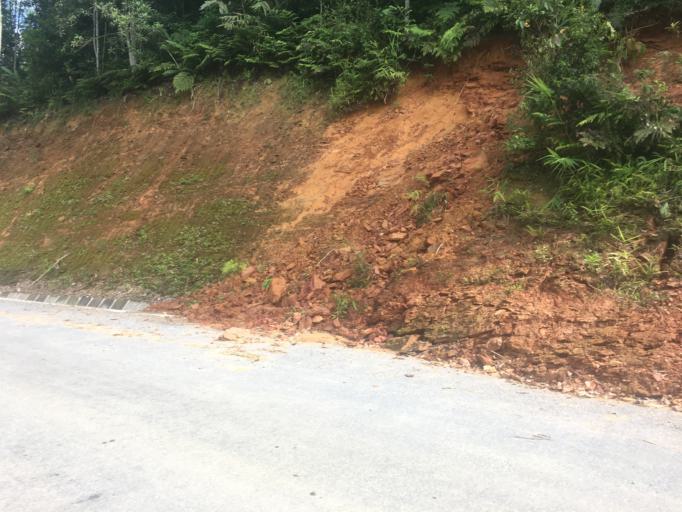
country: VN
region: Ha Giang
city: Thanh Pho Ha Giang
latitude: 22.8566
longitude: 105.0393
